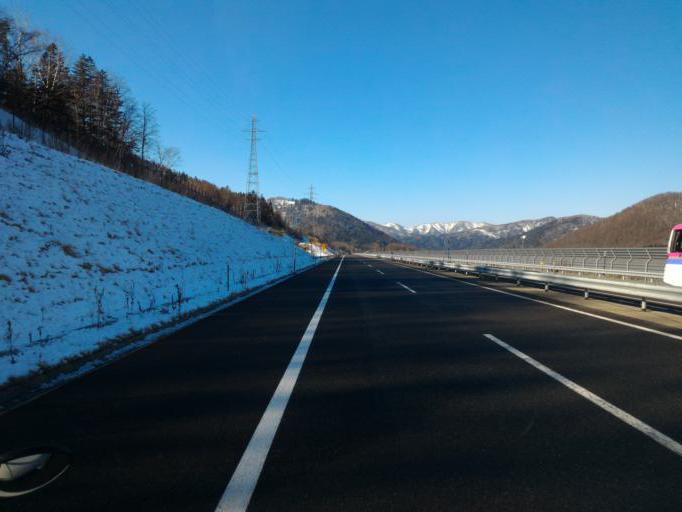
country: JP
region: Hokkaido
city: Shimo-furano
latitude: 43.0530
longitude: 142.5820
